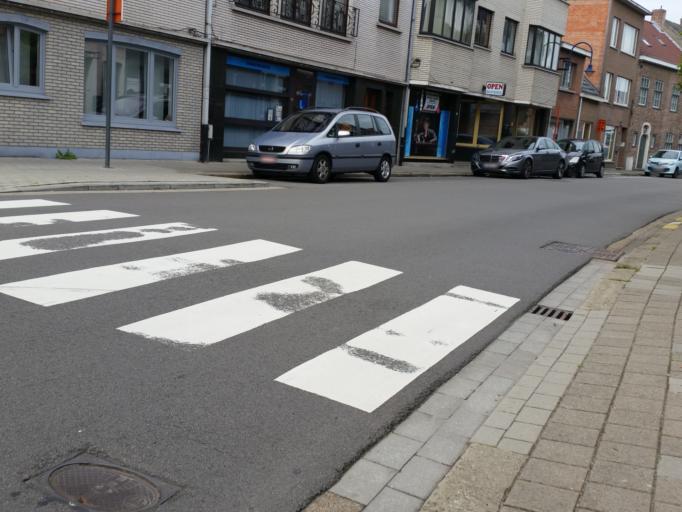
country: BE
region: Flanders
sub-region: Provincie Antwerpen
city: Kontich
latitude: 51.1309
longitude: 4.4464
